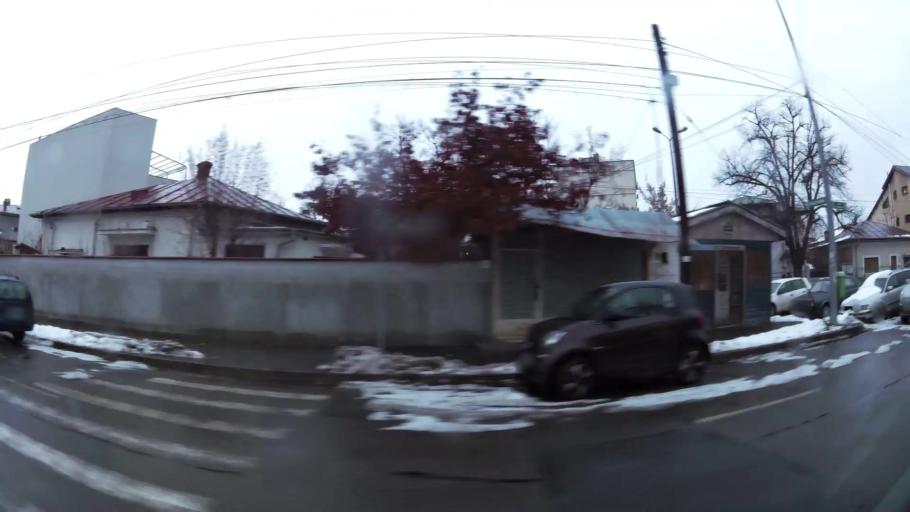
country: RO
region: Ilfov
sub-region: Comuna Chiajna
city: Rosu
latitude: 44.4710
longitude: 26.0580
